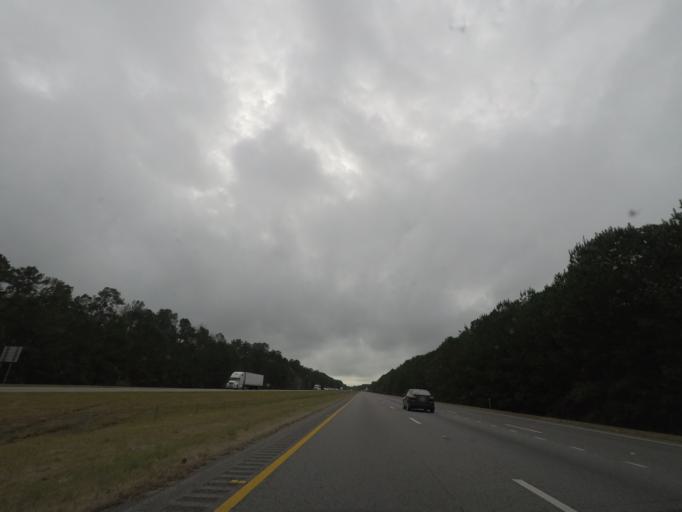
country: US
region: South Carolina
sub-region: Orangeburg County
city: Holly Hill
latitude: 33.4094
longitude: -80.5022
